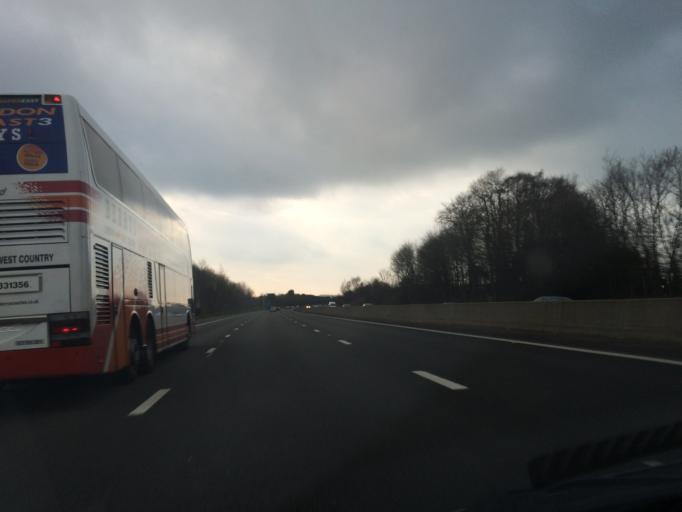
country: GB
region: England
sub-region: West Berkshire
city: Hungerford
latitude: 51.4565
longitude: -1.4937
